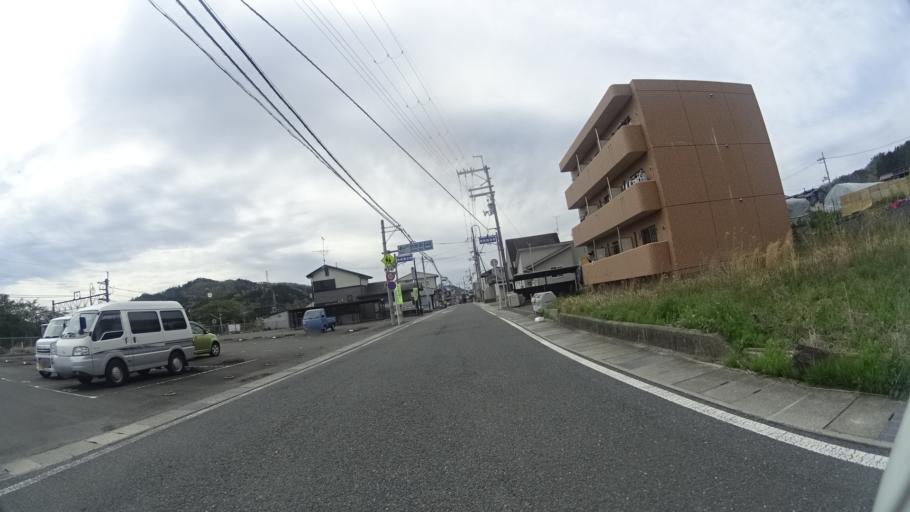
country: JP
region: Kyoto
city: Kameoka
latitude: 35.1953
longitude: 135.4697
